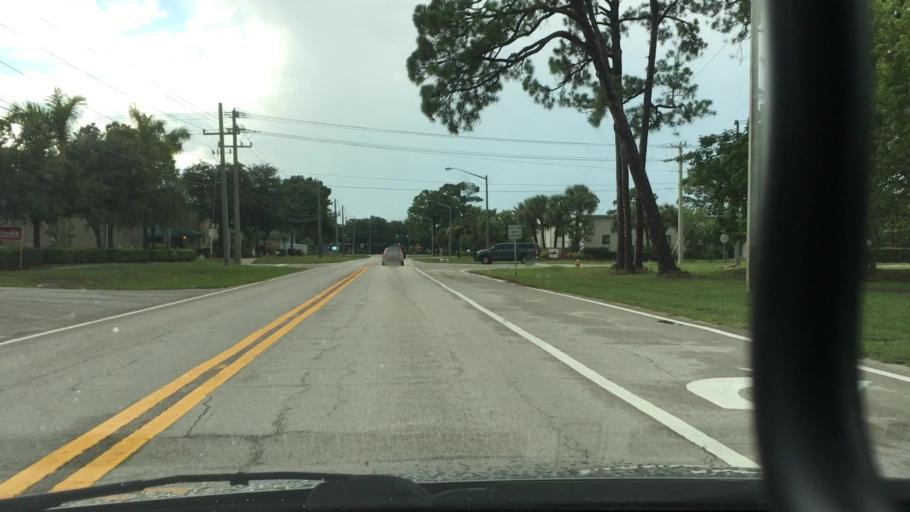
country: US
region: Florida
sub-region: Indian River County
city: Vero Beach
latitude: 27.6466
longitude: -80.4168
